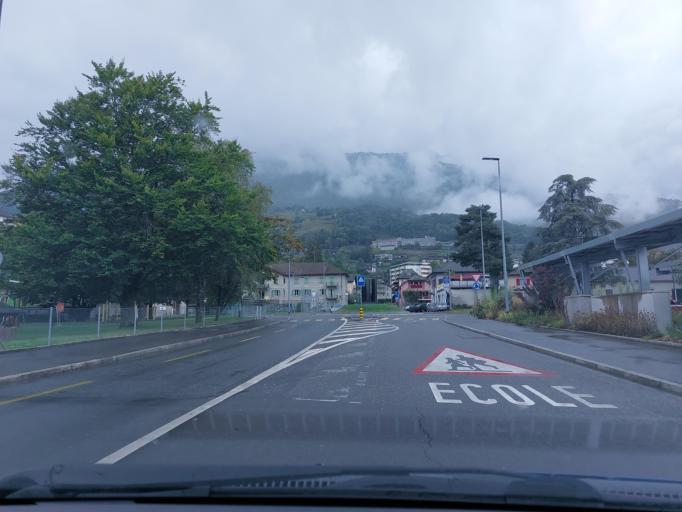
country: CH
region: Valais
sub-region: Monthey District
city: Monthey
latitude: 46.2492
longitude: 6.9510
